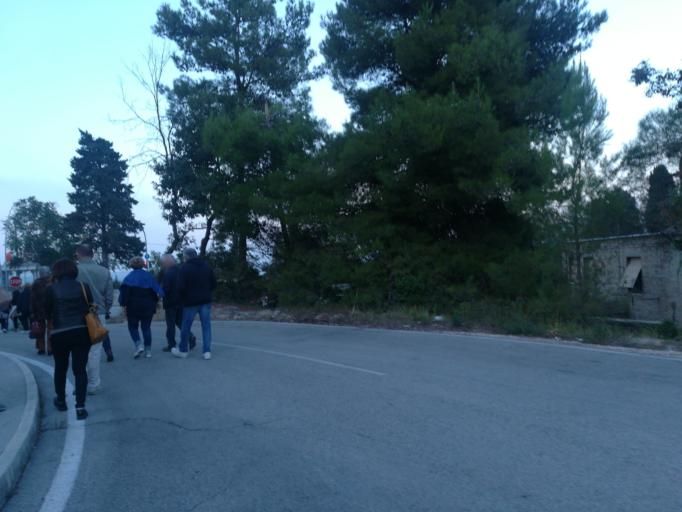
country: IT
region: The Marches
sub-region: Provincia di Macerata
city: Macerata
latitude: 43.2942
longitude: 13.4640
